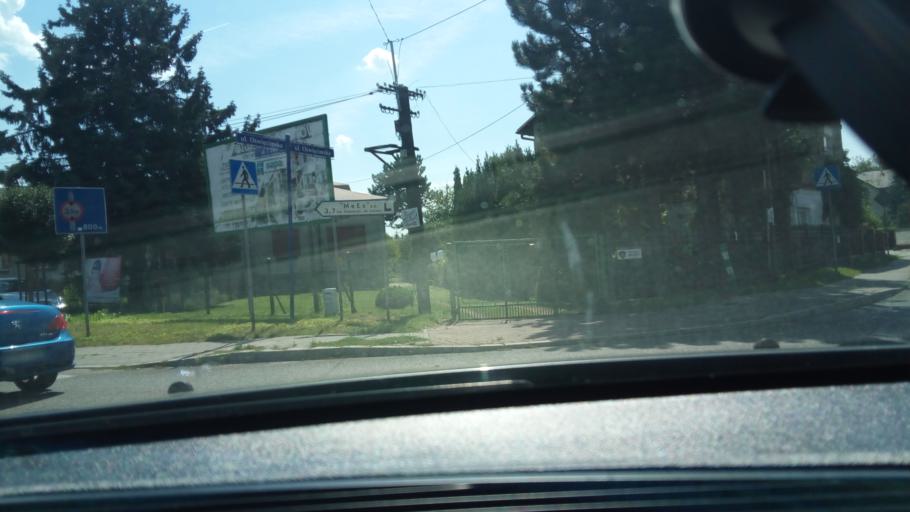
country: PL
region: Lesser Poland Voivodeship
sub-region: Powiat chrzanowski
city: Chrzanow
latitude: 50.1395
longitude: 19.3952
